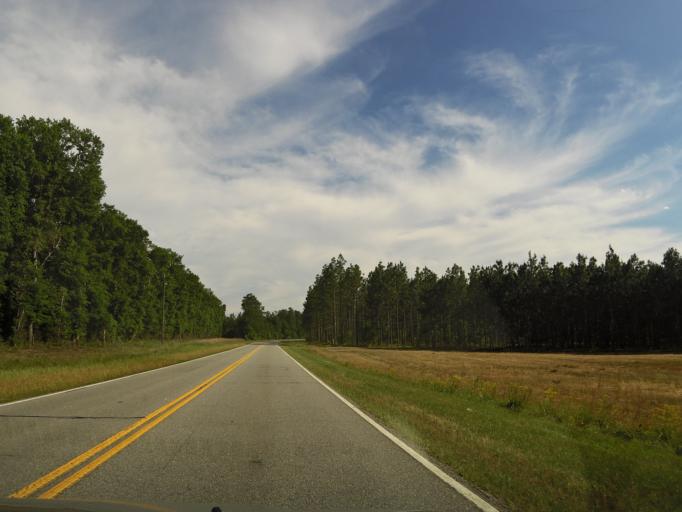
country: US
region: South Carolina
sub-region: Allendale County
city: Allendale
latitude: 33.1224
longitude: -81.1831
